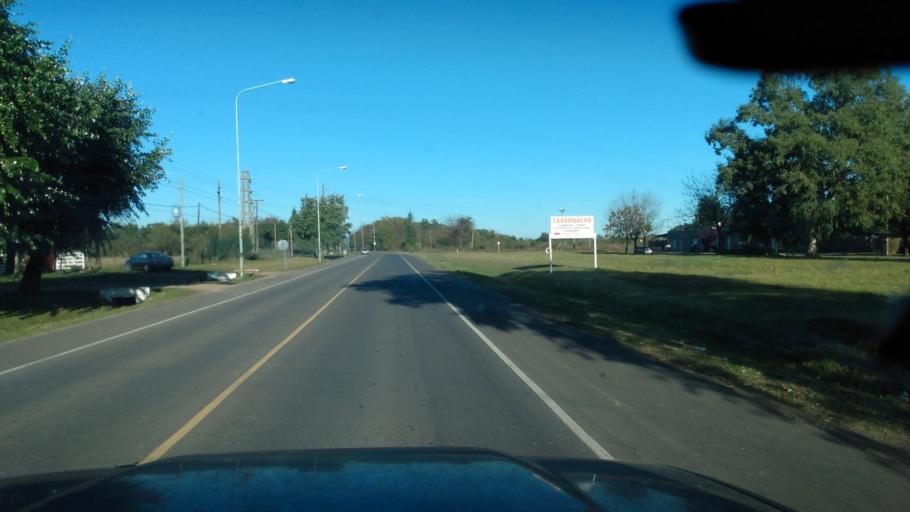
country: AR
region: Buenos Aires
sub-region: Partido de Lujan
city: Lujan
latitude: -34.5635
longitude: -59.1403
